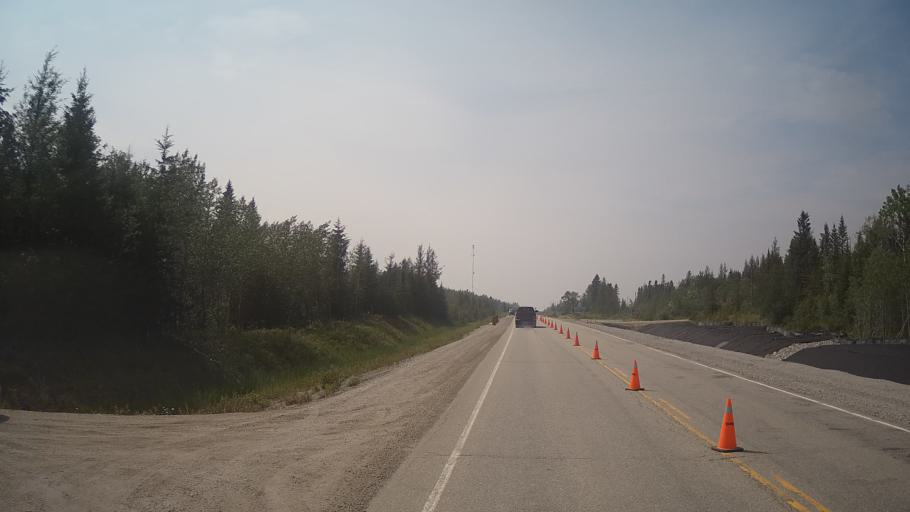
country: CA
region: Ontario
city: Kapuskasing
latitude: 49.3156
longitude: -82.0493
